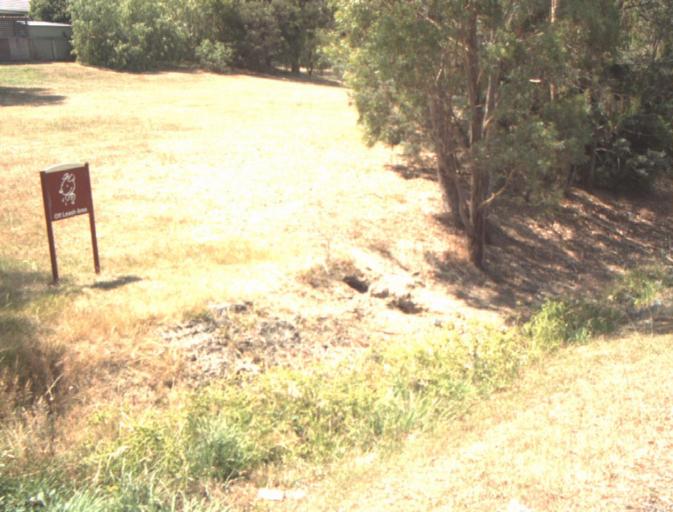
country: AU
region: Tasmania
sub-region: Launceston
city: Newstead
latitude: -41.4721
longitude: 147.1804
